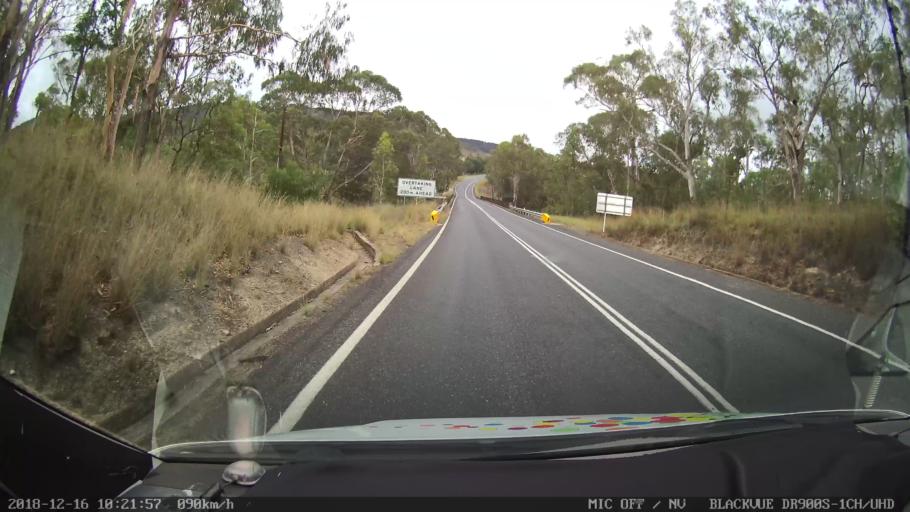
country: AU
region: New South Wales
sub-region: Tenterfield Municipality
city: Carrolls Creek
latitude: -29.2005
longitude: 152.0130
